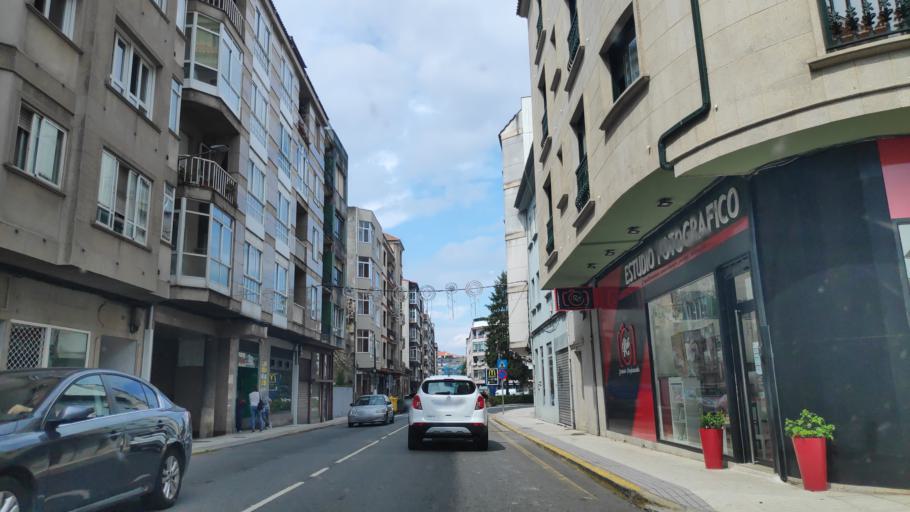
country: ES
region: Galicia
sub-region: Provincia de Pontevedra
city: Vilagarcia de Arousa
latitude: 42.5944
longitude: -8.7614
